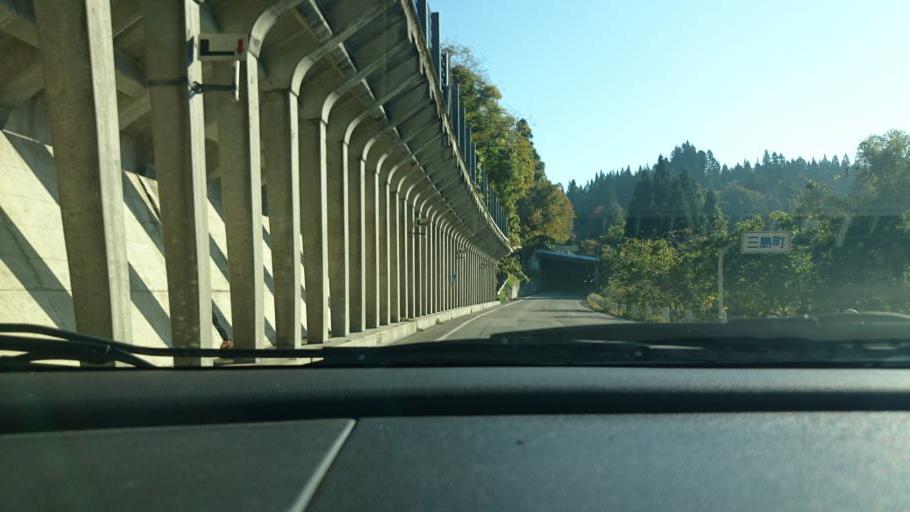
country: JP
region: Fukushima
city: Kitakata
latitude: 37.4976
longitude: 139.6850
